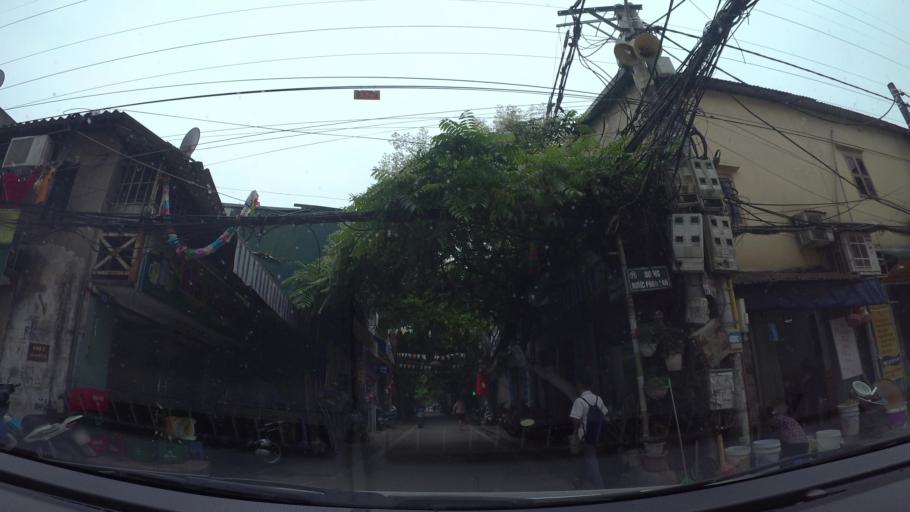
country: VN
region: Ha Noi
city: Tay Ho
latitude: 21.0670
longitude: 105.8335
